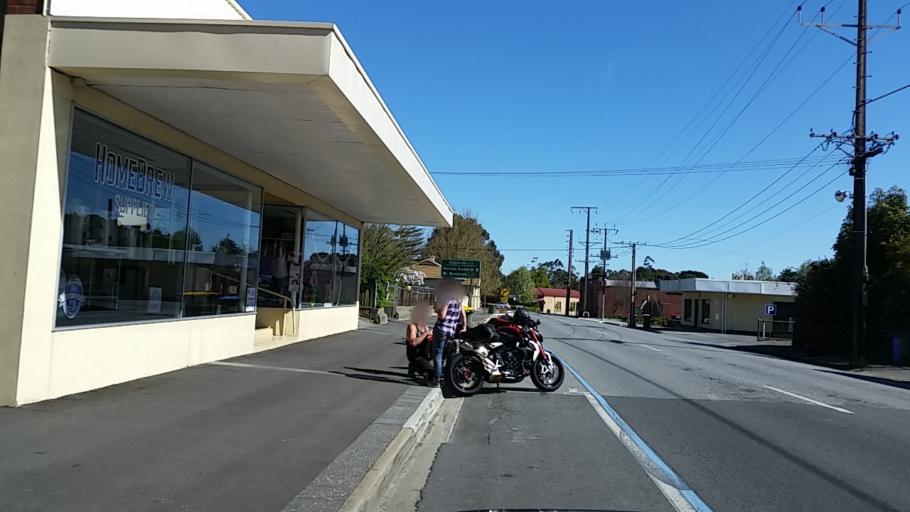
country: AU
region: South Australia
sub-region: Adelaide Hills
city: Lobethal
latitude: -34.9068
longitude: 138.8739
